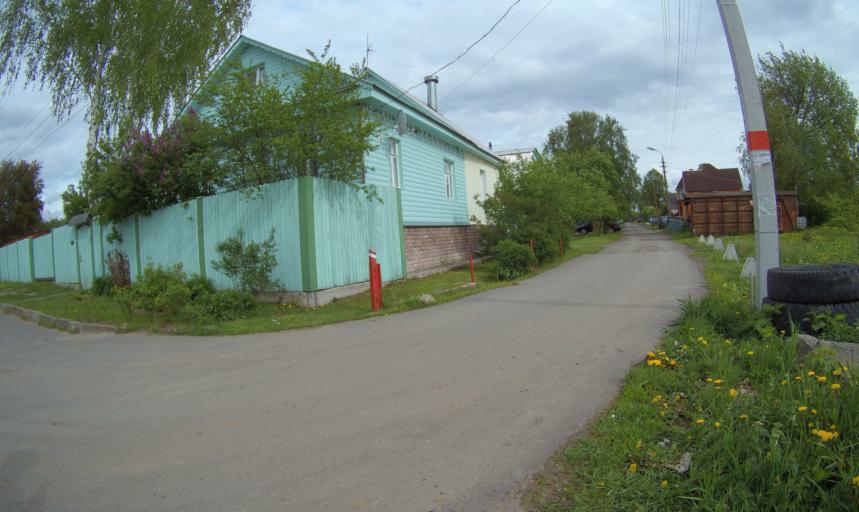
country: RU
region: Moskovskaya
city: Kolomna
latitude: 55.0998
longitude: 38.7449
